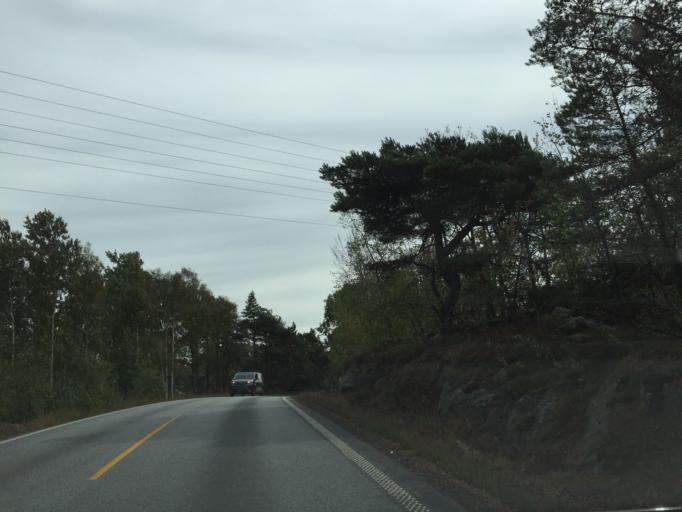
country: NO
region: Ostfold
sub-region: Hvaler
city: Skjaerhalden
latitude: 59.0657
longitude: 10.9373
